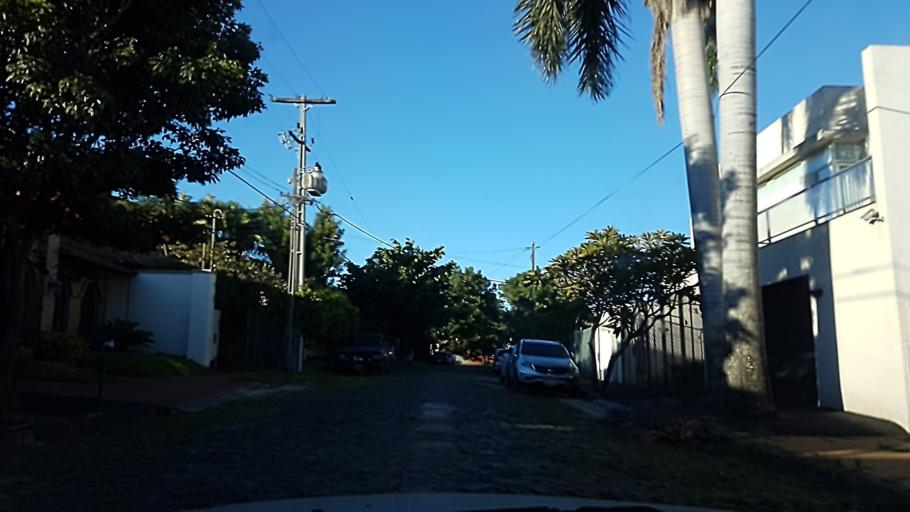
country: PY
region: Asuncion
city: Asuncion
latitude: -25.2662
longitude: -57.5628
